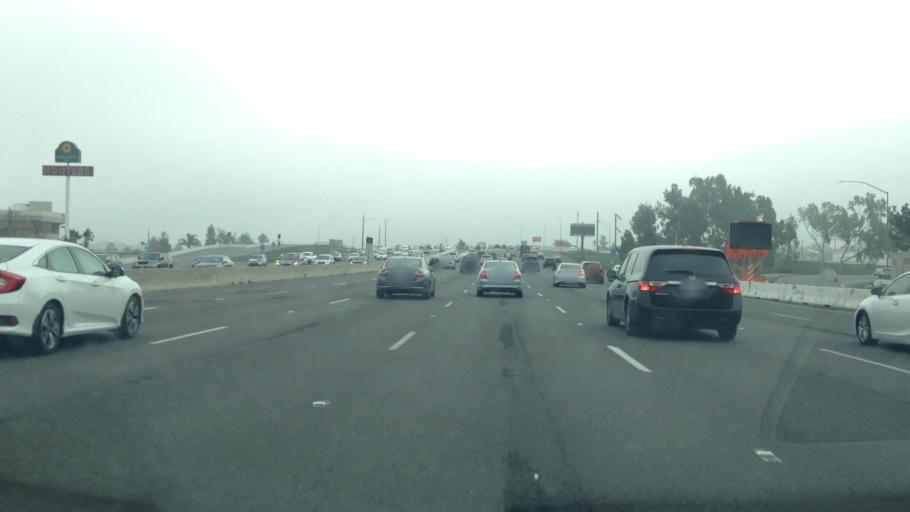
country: US
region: California
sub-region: Orange County
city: Fountain Valley
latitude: 33.6905
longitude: -117.9230
